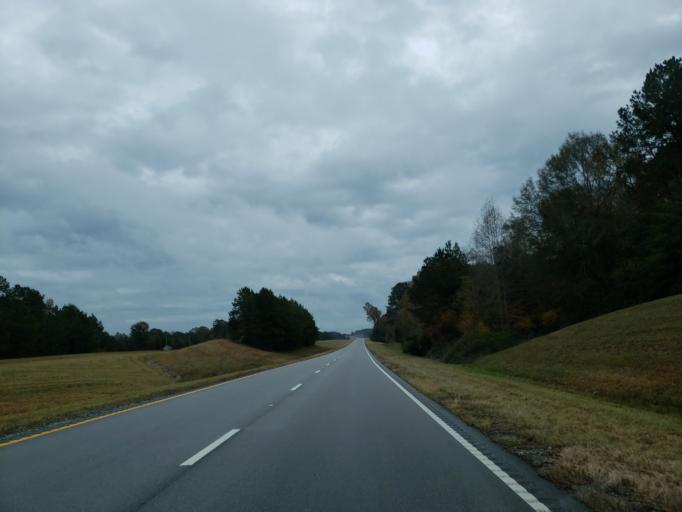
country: US
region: Mississippi
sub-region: Wayne County
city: Waynesboro
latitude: 31.6947
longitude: -88.7198
